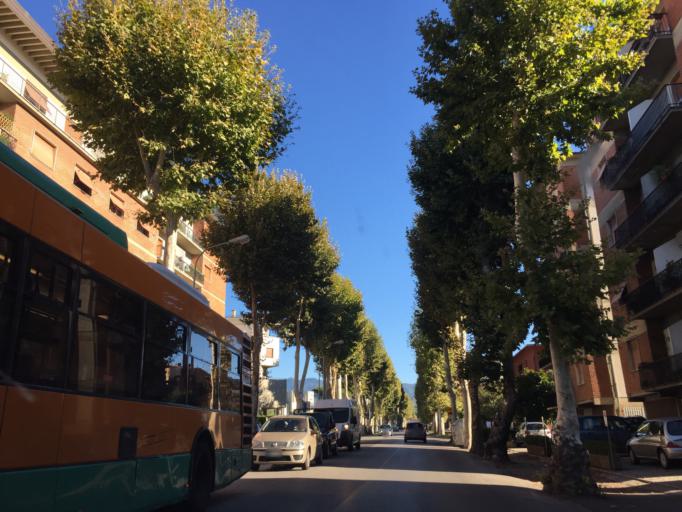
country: IT
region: Tuscany
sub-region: Provincia di Pistoia
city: Pistoia
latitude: 43.9401
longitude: 10.9007
